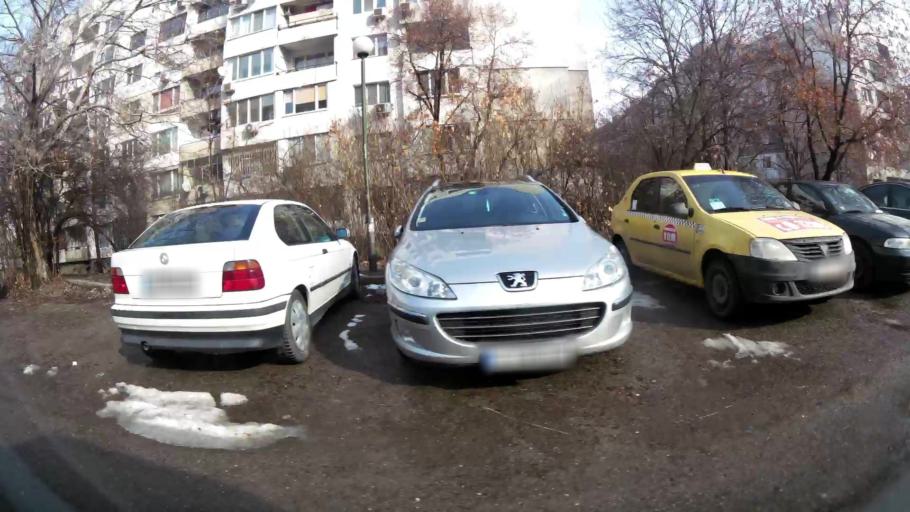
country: BG
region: Sofia-Capital
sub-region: Stolichna Obshtina
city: Sofia
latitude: 42.7163
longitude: 23.2641
